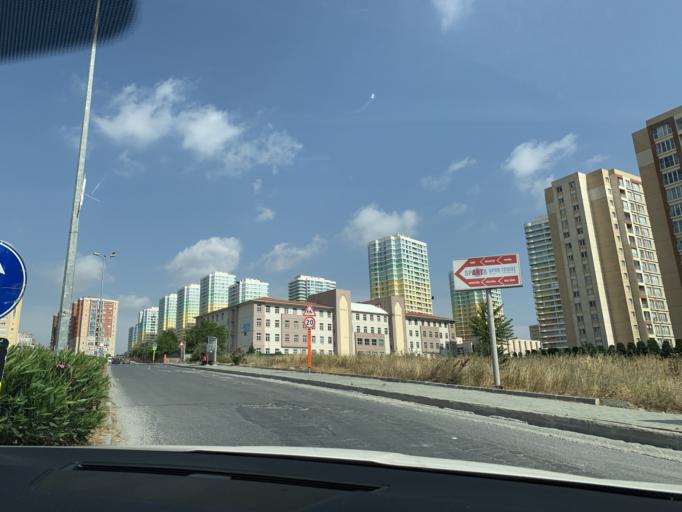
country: TR
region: Istanbul
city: Esenyurt
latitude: 41.0655
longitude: 28.7060
